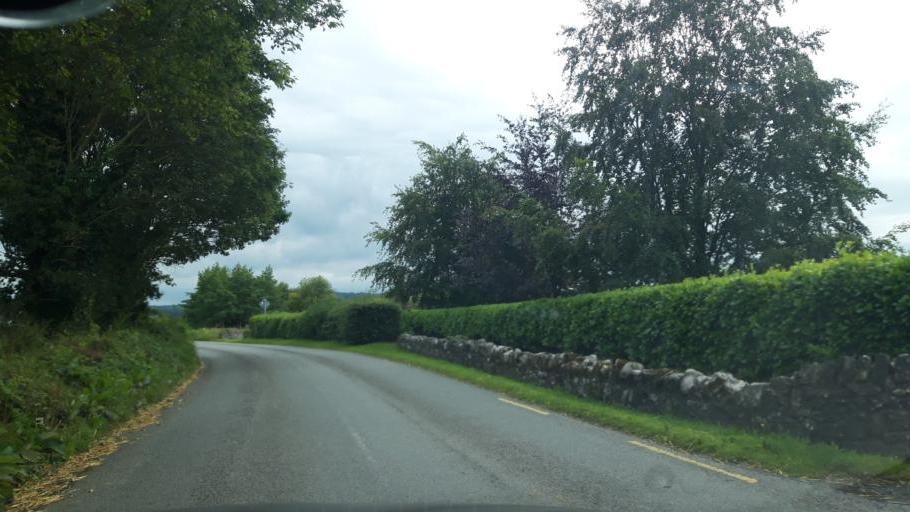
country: IE
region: Leinster
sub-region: Kilkenny
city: Ballyragget
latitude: 52.7432
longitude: -7.3984
